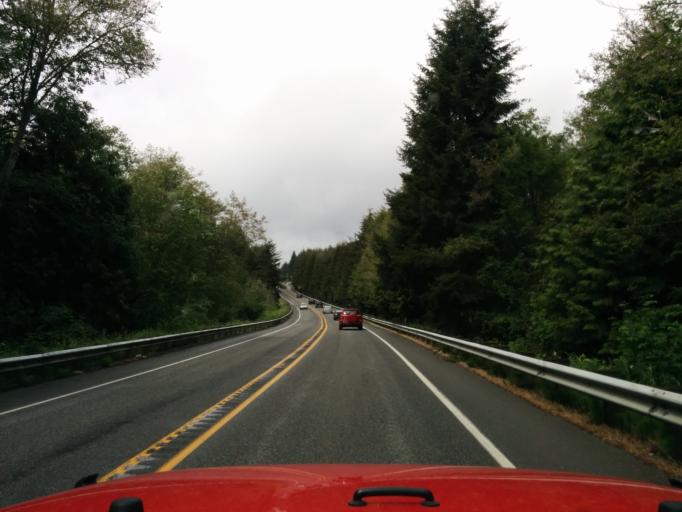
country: US
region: Washington
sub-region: Island County
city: Langley
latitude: 47.9999
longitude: -122.4081
